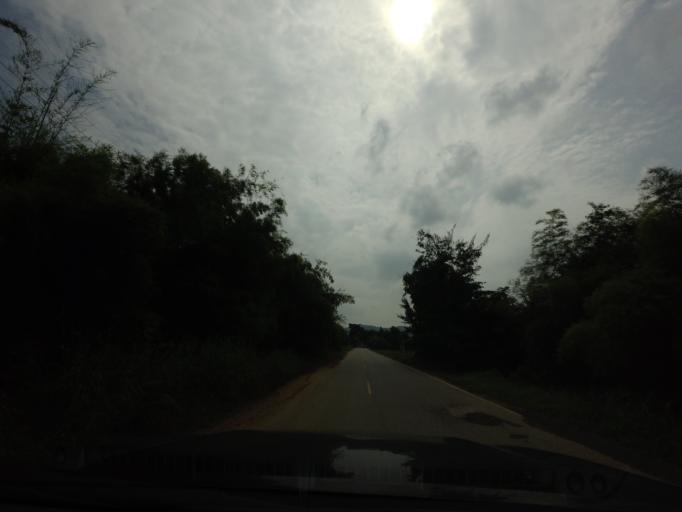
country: TH
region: Loei
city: Tha Li
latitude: 17.6539
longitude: 101.3654
